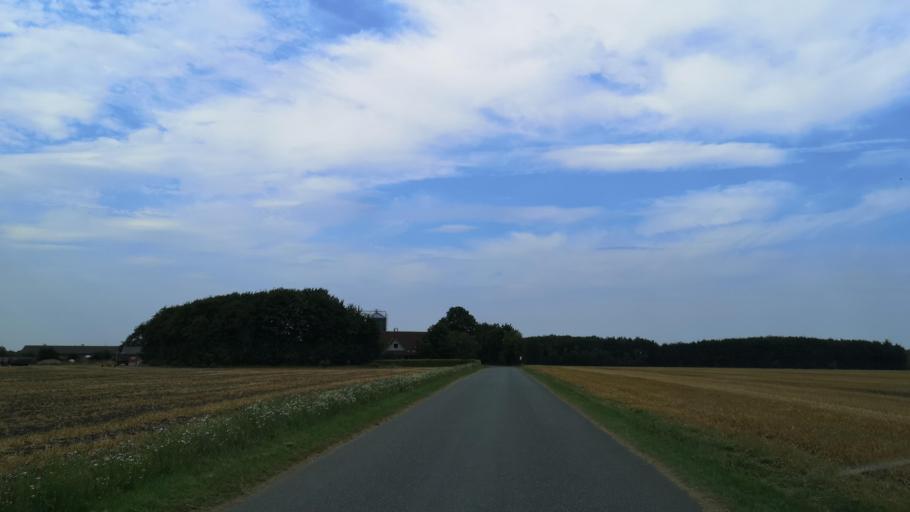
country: DK
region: Central Jutland
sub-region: Ringkobing-Skjern Kommune
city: Videbaek
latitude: 56.0788
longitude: 8.6840
